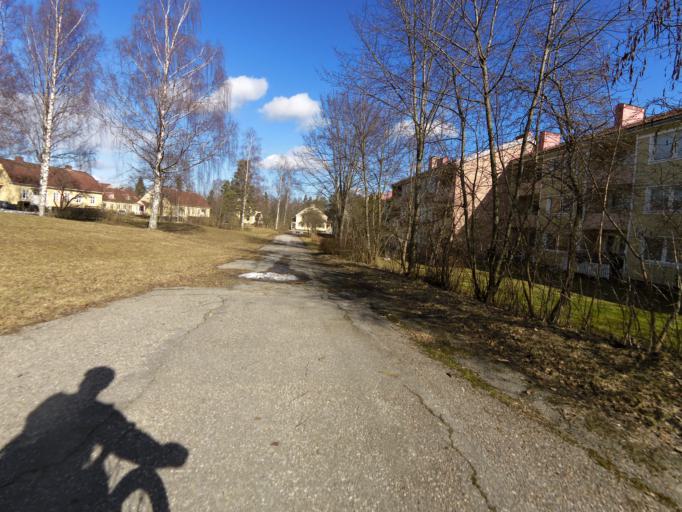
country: SE
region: Gaevleborg
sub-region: Hofors Kommun
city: Hofors
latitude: 60.5466
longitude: 16.2909
